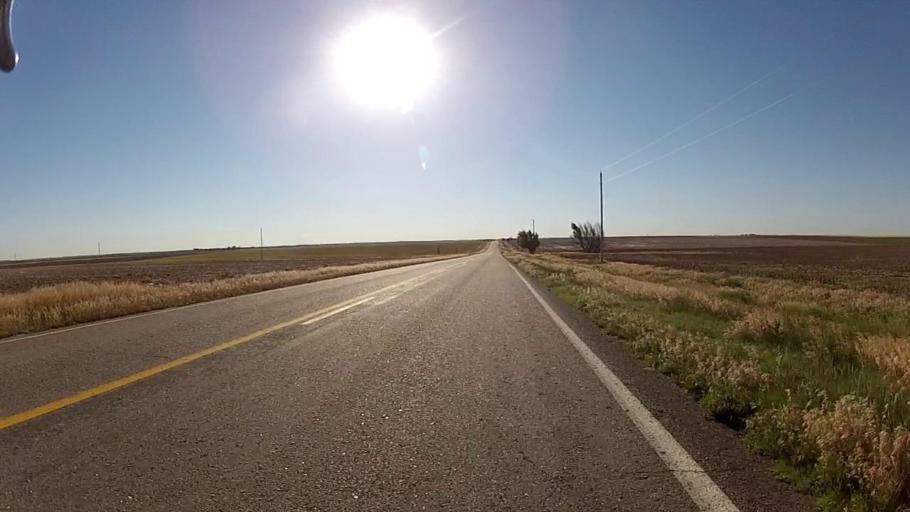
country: US
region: Kansas
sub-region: Ford County
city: Dodge City
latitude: 37.6462
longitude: -99.8352
